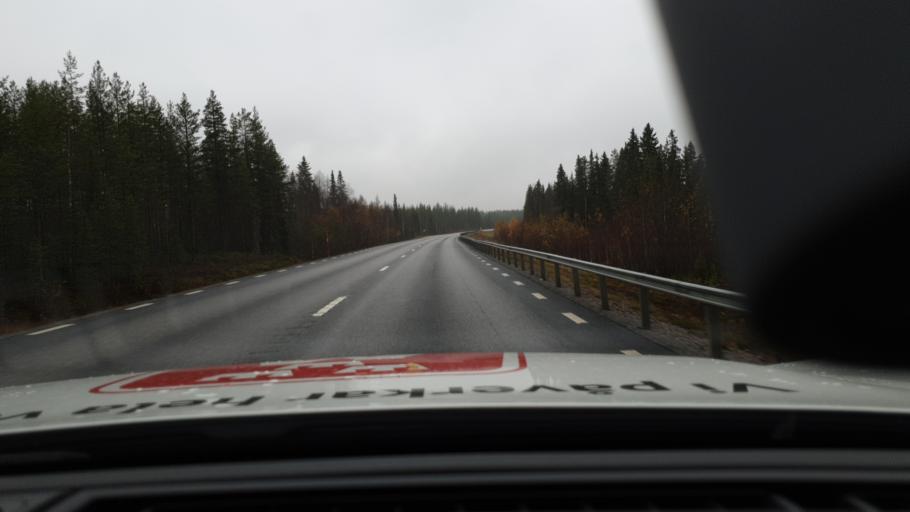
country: SE
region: Norrbotten
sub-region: Overkalix Kommun
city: OEverkalix
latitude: 66.6310
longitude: 22.2103
